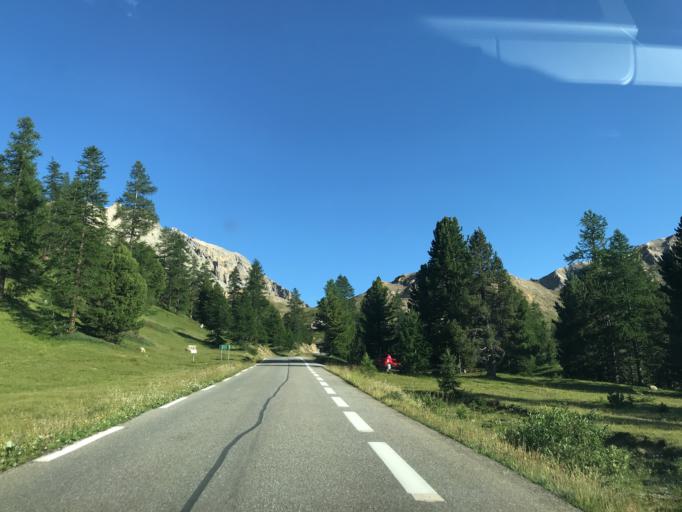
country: FR
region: Provence-Alpes-Cote d'Azur
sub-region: Departement des Hautes-Alpes
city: Villar-Saint-Pancrace
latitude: 44.8265
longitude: 6.7300
